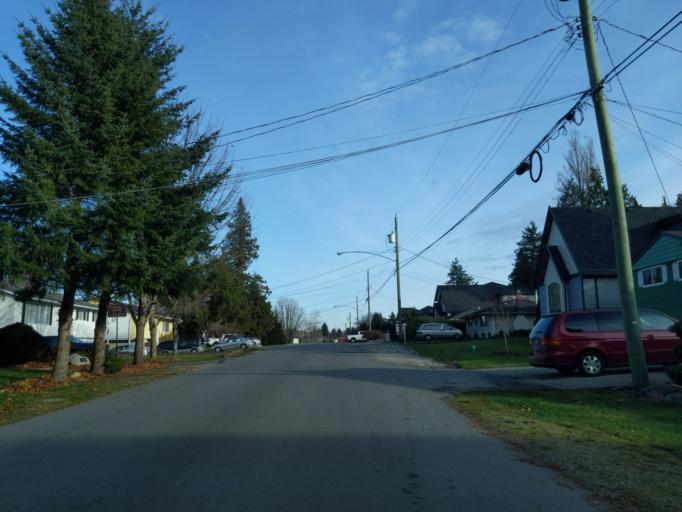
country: CA
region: British Columbia
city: New Westminster
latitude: 49.1970
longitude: -122.8605
